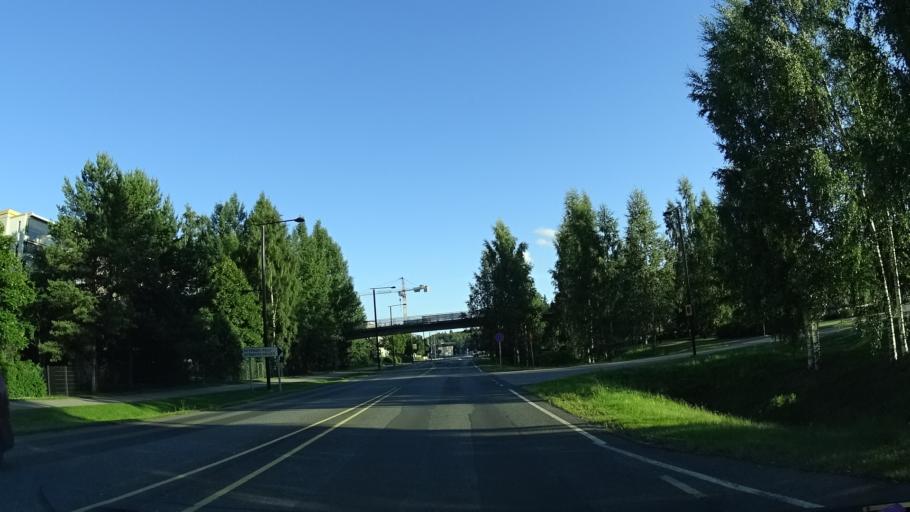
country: FI
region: Uusimaa
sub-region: Helsinki
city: Teekkarikylae
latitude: 60.2627
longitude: 24.8430
